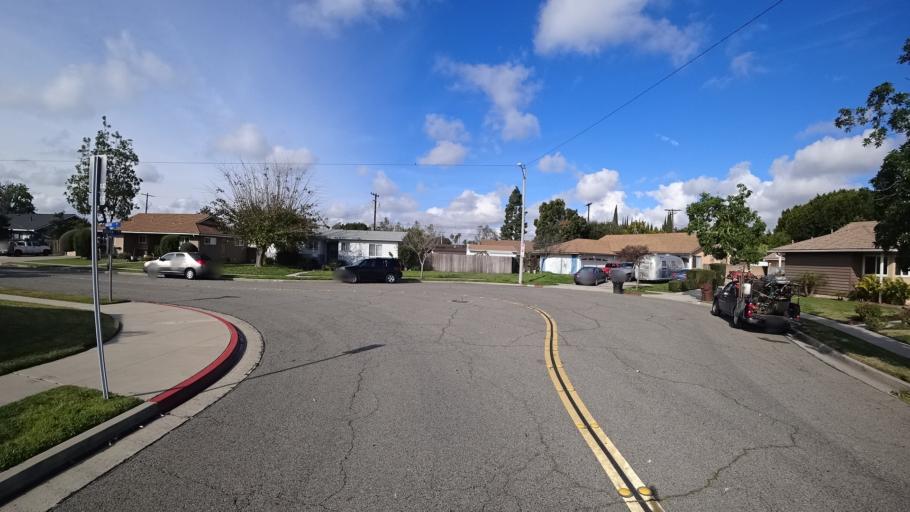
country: US
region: California
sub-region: Orange County
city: Stanton
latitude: 33.8256
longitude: -117.9748
